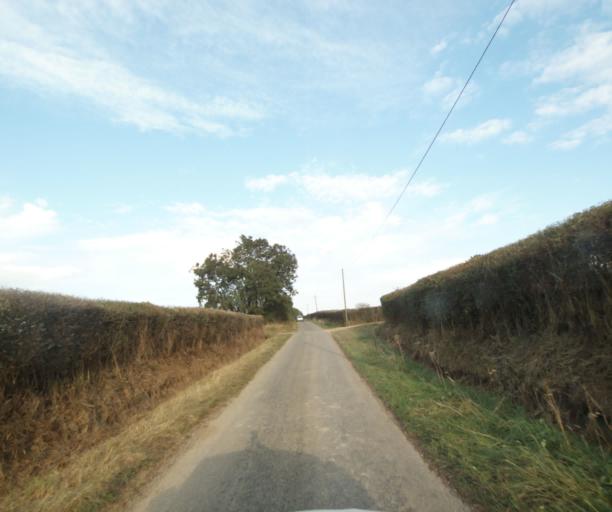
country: FR
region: Bourgogne
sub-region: Departement de Saone-et-Loire
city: Charolles
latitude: 46.4380
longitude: 4.3584
